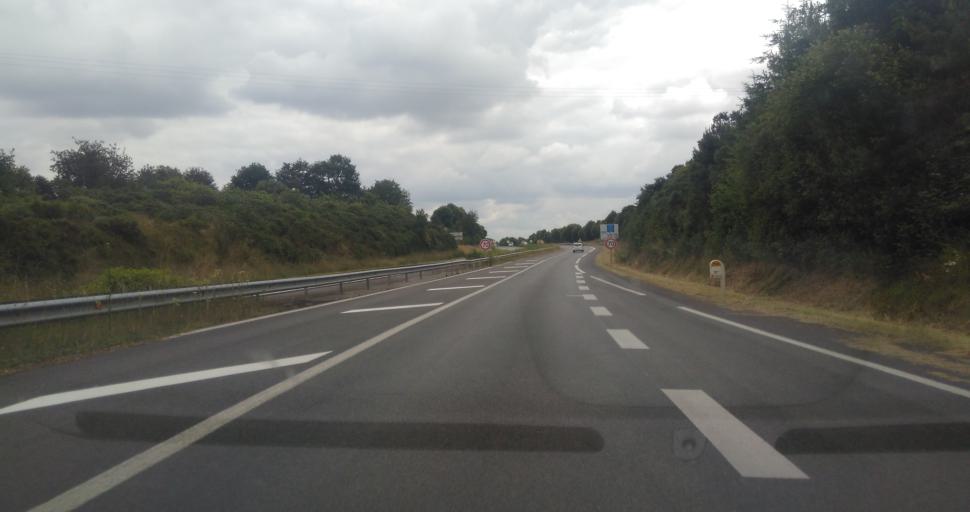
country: FR
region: Pays de la Loire
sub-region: Departement de la Vendee
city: Bournezeau
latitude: 46.6289
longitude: -1.1681
